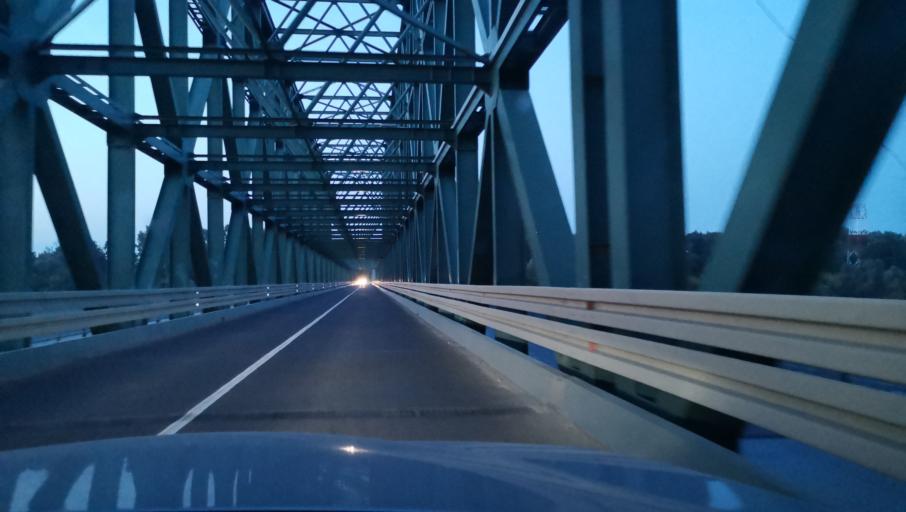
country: RS
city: Zvecka
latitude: 44.6731
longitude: 20.1665
